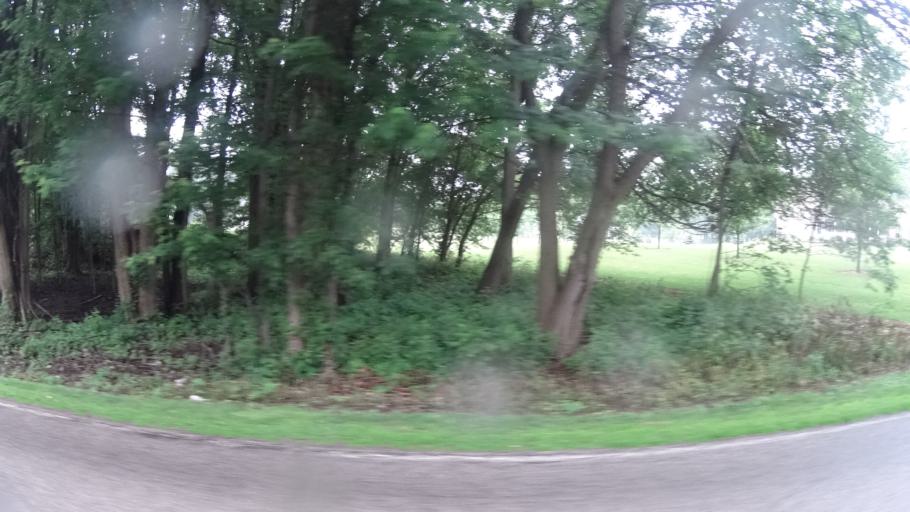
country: US
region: Ohio
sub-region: Huron County
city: Bellevue
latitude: 41.3707
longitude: -82.8450
